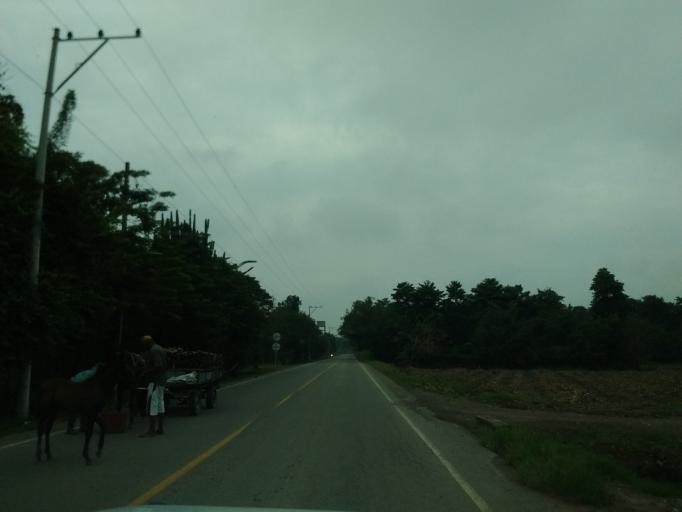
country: CO
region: Cauca
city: Padilla
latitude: 3.2259
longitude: -76.3536
